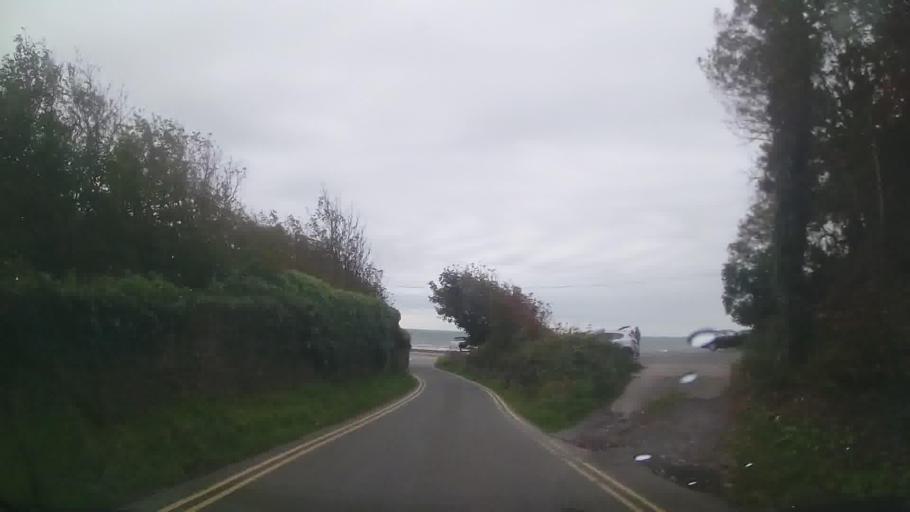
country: GB
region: Wales
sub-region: Pembrokeshire
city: Saundersfoot
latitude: 51.7336
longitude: -4.6559
